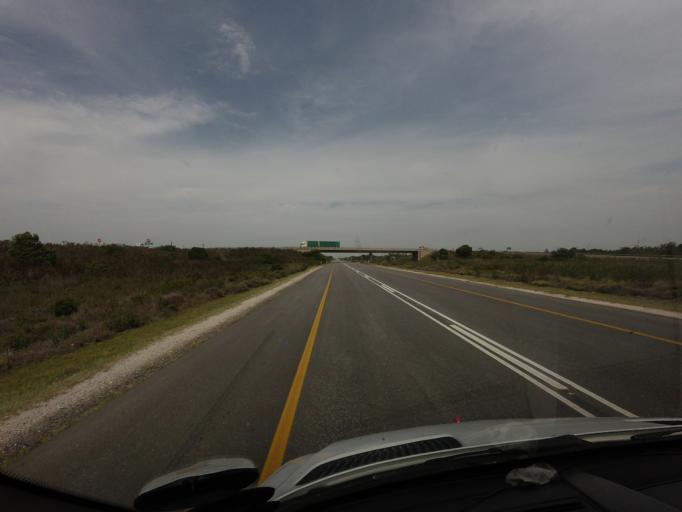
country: ZA
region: Eastern Cape
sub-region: Cacadu District Municipality
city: Kruisfontein
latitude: -34.0063
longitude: 24.7781
